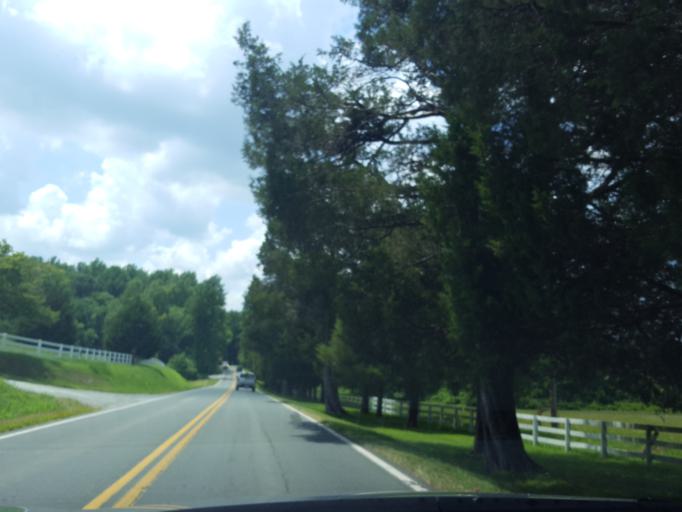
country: US
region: Virginia
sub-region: Orange County
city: Gordonsville
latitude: 38.0675
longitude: -78.3038
